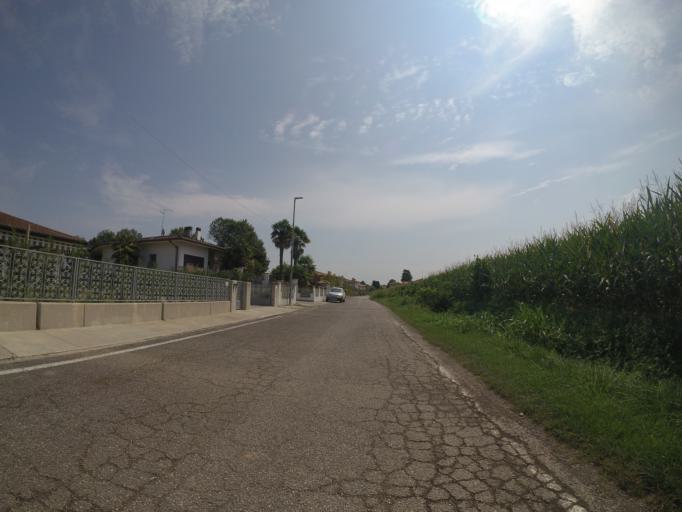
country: IT
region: Friuli Venezia Giulia
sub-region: Provincia di Udine
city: Varmo
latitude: 45.8998
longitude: 13.0148
